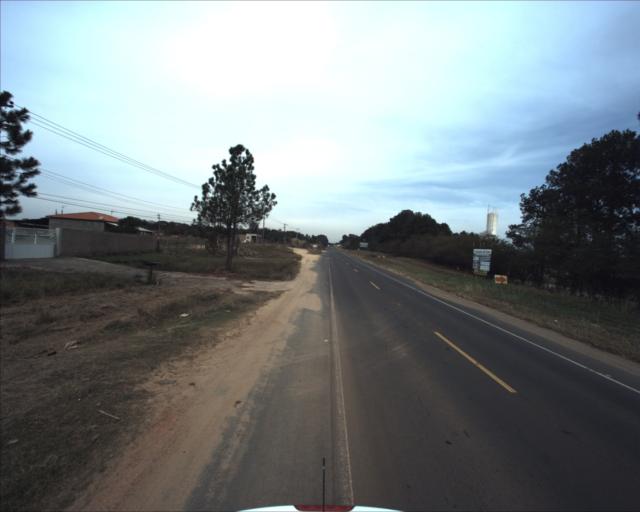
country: BR
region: Sao Paulo
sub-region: Sorocaba
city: Sorocaba
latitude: -23.4031
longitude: -47.5180
